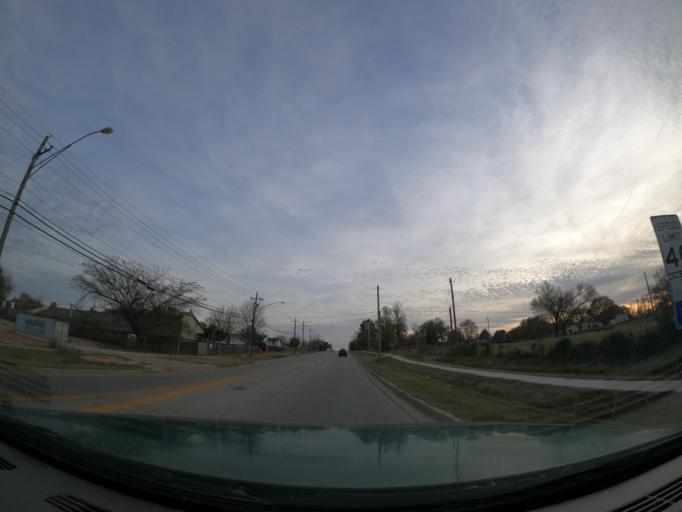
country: US
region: Oklahoma
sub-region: Tulsa County
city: Broken Arrow
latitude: 35.9866
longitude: -95.7974
